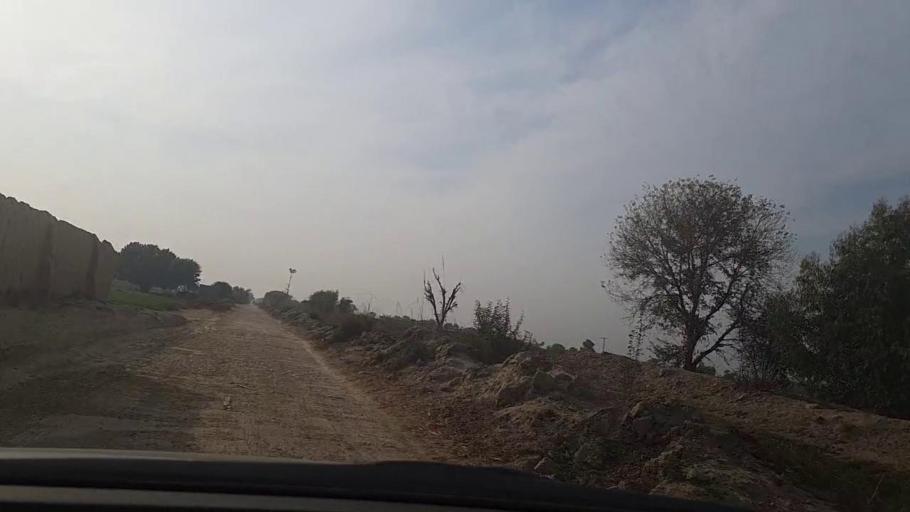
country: PK
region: Sindh
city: Daulatpur
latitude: 26.3340
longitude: 68.0731
